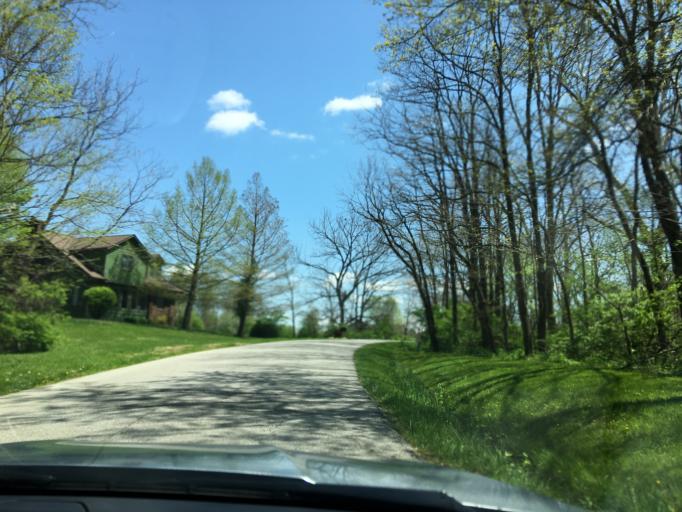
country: US
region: Indiana
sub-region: Tippecanoe County
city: Dayton
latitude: 40.3135
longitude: -86.7468
